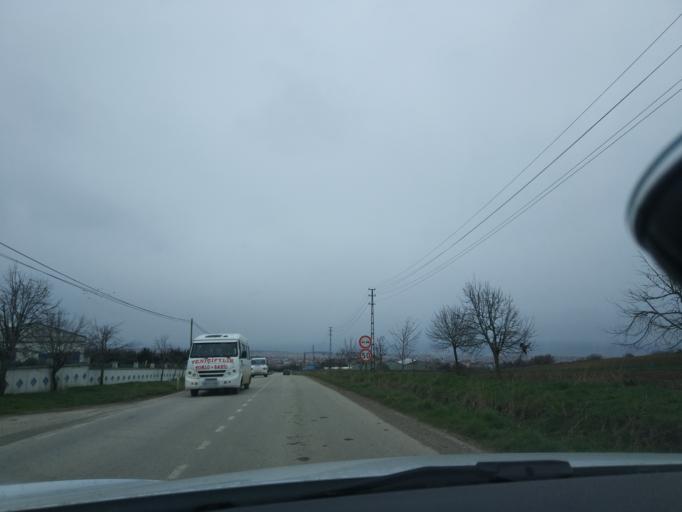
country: TR
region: Tekirdag
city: Marmara Ereglisi
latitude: 41.0233
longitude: 27.8529
